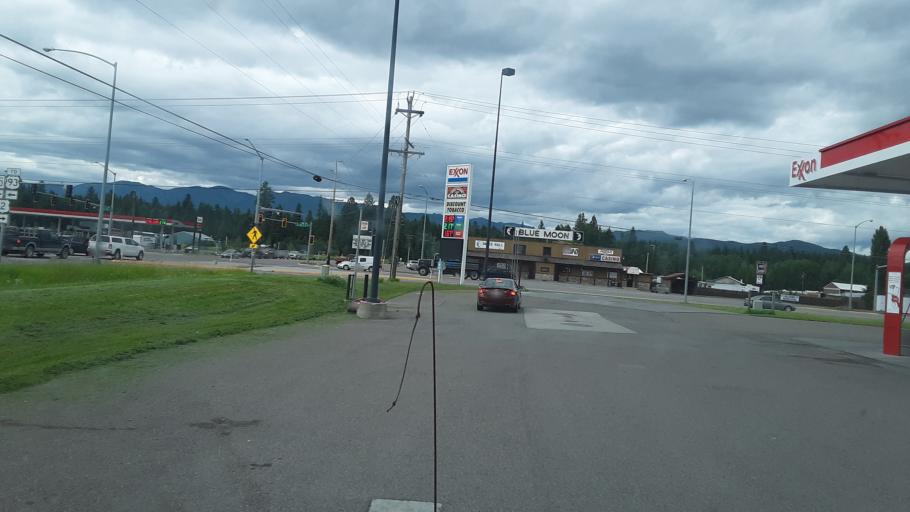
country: US
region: Montana
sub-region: Flathead County
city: Columbia Falls
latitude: 48.3699
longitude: -114.2404
